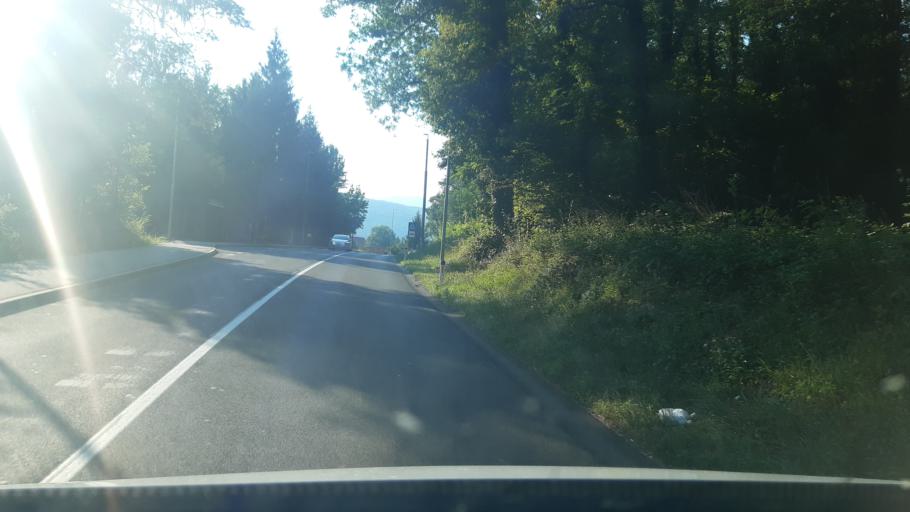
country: SI
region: Crnomelj
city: Crnomelj
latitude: 45.5884
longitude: 15.1811
